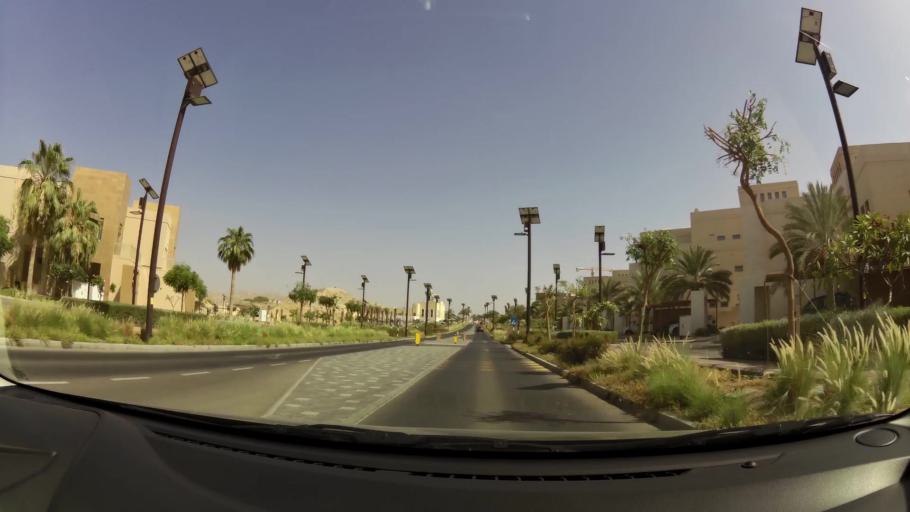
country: OM
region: Muhafazat Masqat
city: Muscat
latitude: 23.6278
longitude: 58.5032
